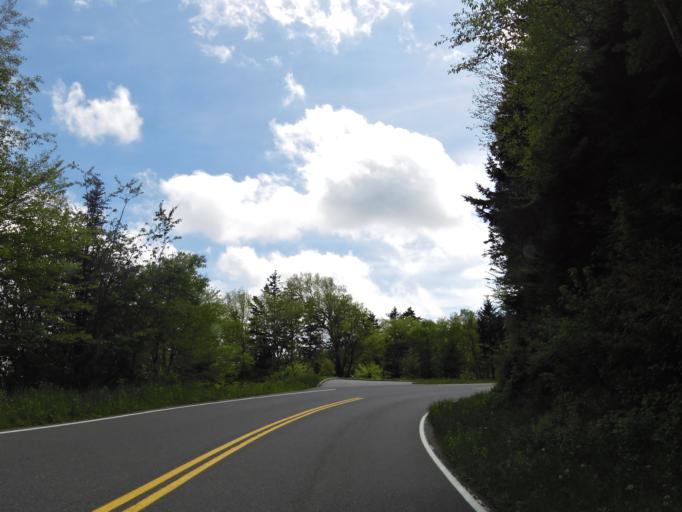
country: US
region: Tennessee
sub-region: Sevier County
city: Gatlinburg
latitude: 35.6100
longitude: -83.4439
